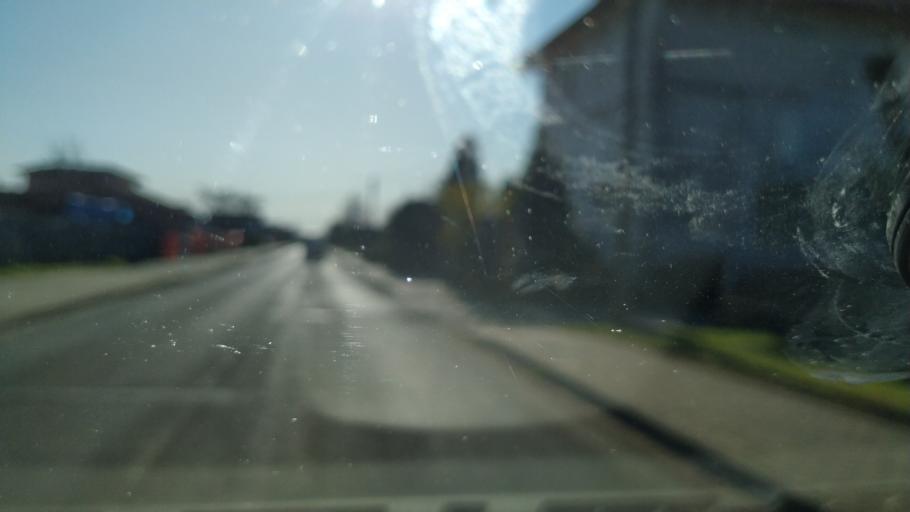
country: IT
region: Piedmont
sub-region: Provincia di Vercelli
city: Lozzolo
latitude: 45.6181
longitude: 8.3227
